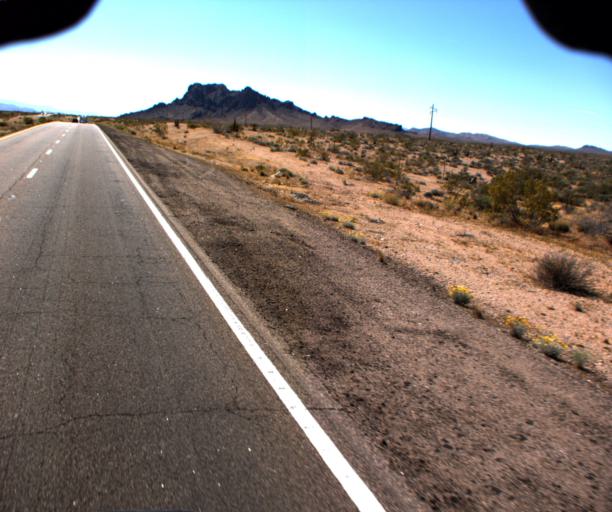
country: US
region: Nevada
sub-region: Clark County
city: Boulder City
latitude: 35.8142
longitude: -114.5476
